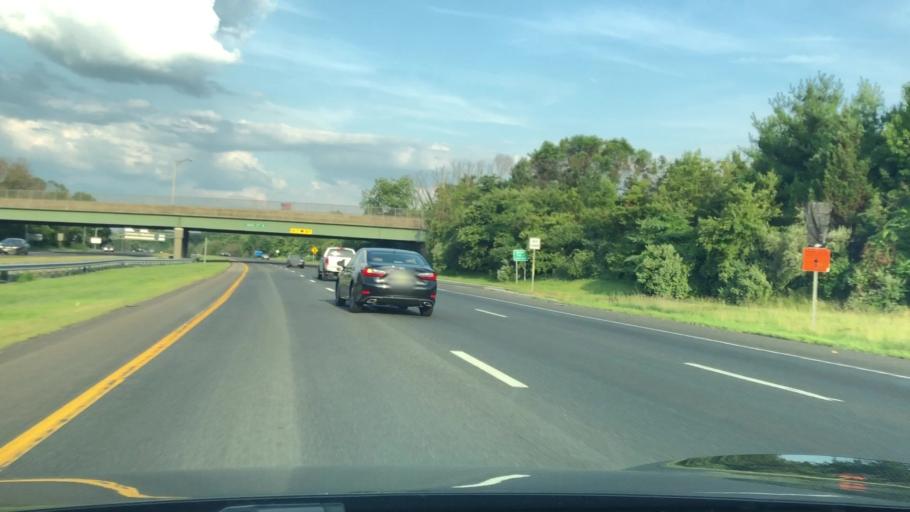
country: US
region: New Jersey
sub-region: Mercer County
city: Lawrenceville
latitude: 40.2879
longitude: -74.7611
